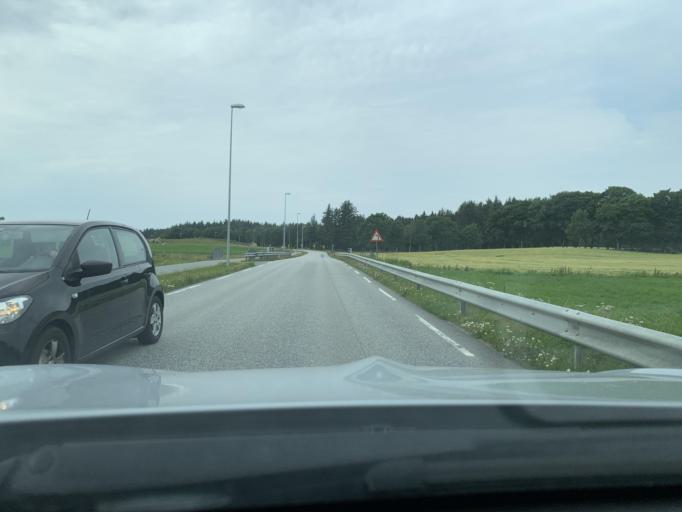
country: NO
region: Rogaland
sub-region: Time
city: Bryne
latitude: 58.7552
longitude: 5.7035
